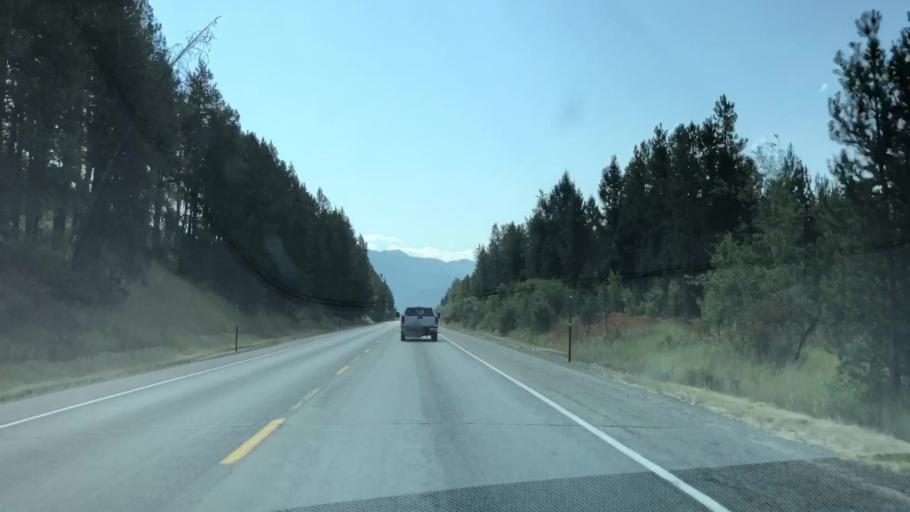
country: US
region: Wyoming
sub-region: Teton County
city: Hoback
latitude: 43.2002
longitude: -111.0436
